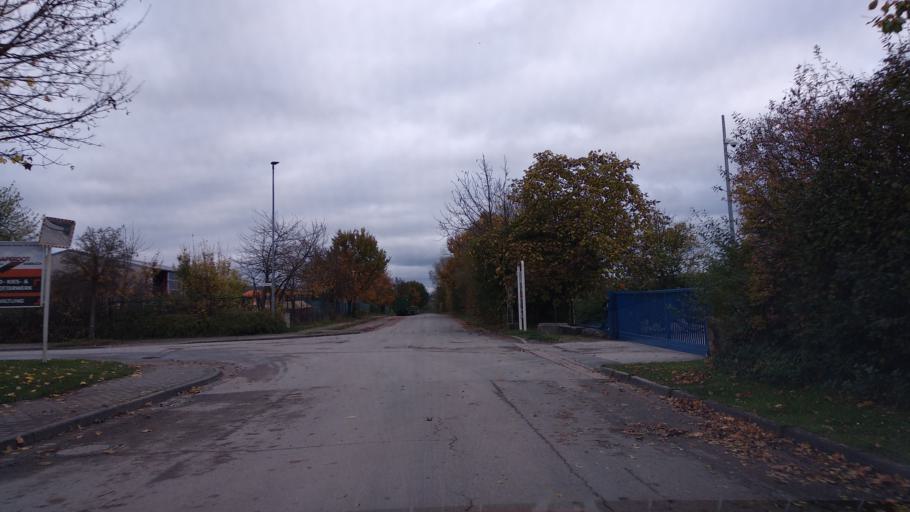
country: DE
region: North Rhine-Westphalia
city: Beverungen
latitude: 51.6749
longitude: 9.3842
